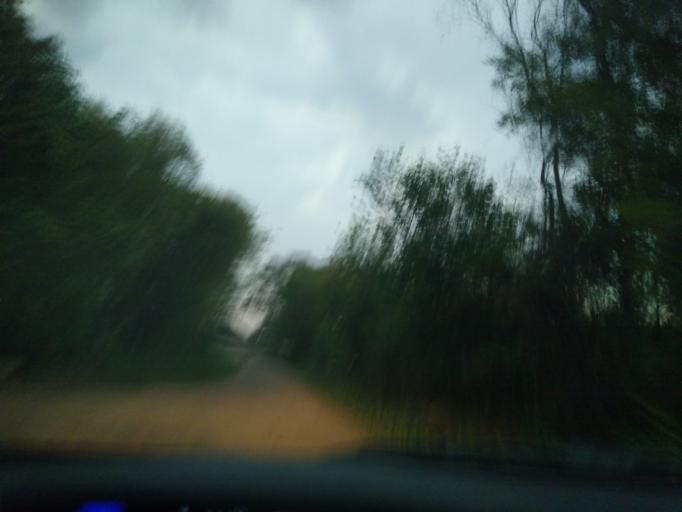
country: AR
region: Chaco
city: Puerto Tirol
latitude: -27.3749
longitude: -59.0827
